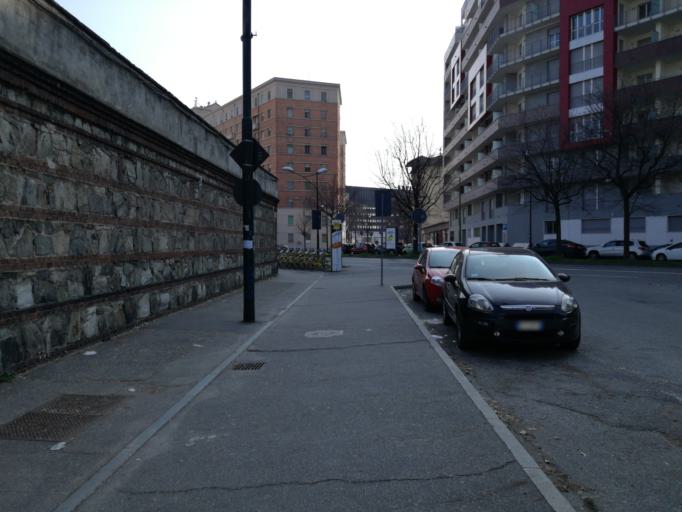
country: IT
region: Piedmont
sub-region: Provincia di Torino
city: Turin
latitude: 45.0642
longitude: 7.6560
